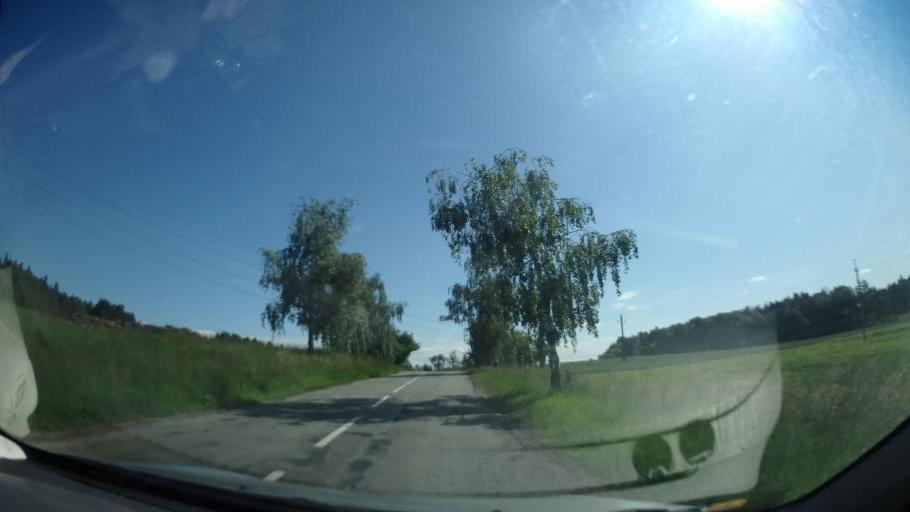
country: CZ
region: South Moravian
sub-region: Okres Blansko
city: Letovice
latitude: 49.6005
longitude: 16.6045
